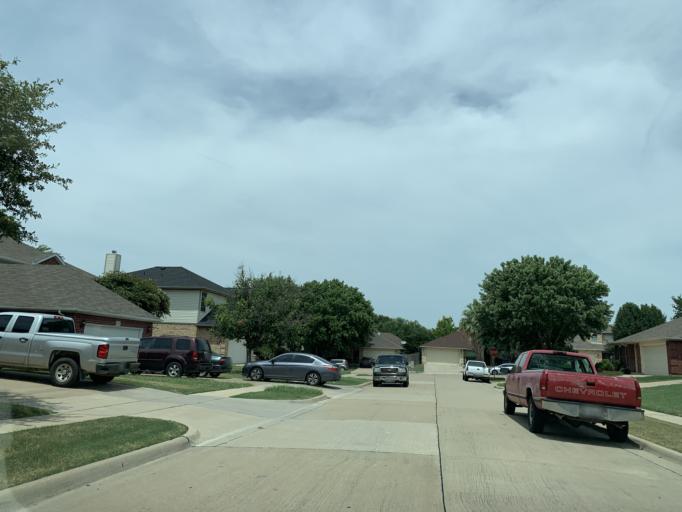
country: US
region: Texas
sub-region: Dallas County
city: Grand Prairie
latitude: 32.6639
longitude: -97.0168
